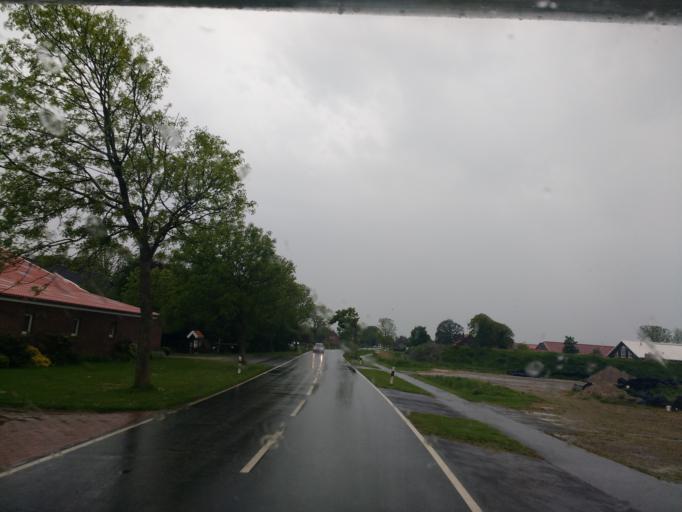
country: DE
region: Lower Saxony
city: Schillig
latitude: 53.7045
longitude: 7.9316
